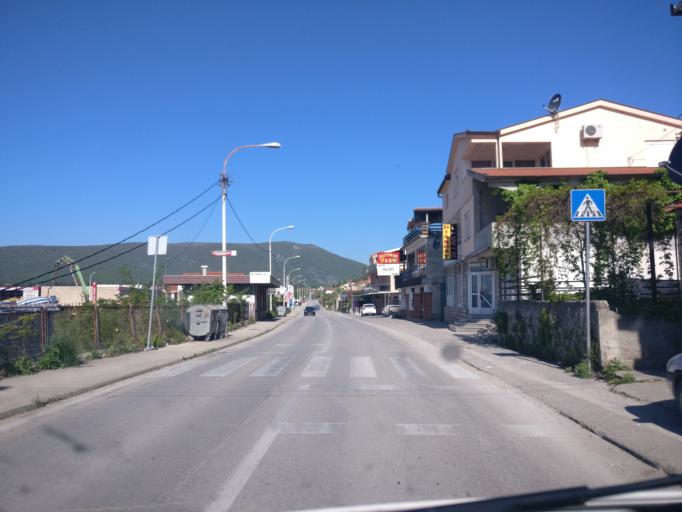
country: BA
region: Federation of Bosnia and Herzegovina
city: Capljina
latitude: 43.1167
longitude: 17.6987
